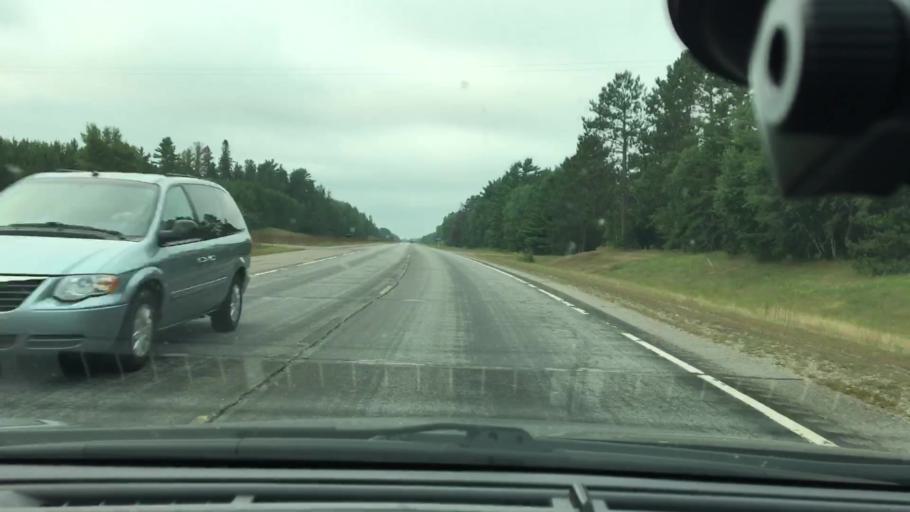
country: US
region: Minnesota
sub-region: Crow Wing County
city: Cross Lake
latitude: 46.7100
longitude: -93.9562
